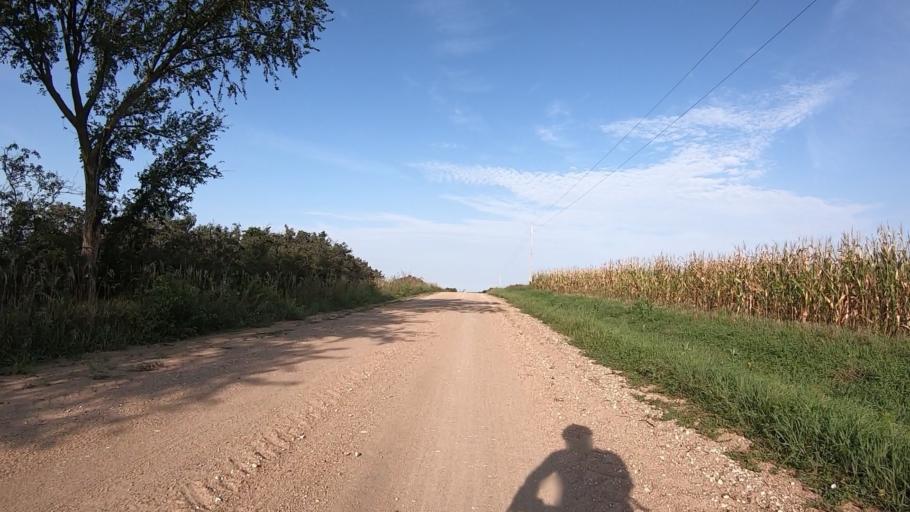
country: US
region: Kansas
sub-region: Marshall County
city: Blue Rapids
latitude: 39.6533
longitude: -96.8481
